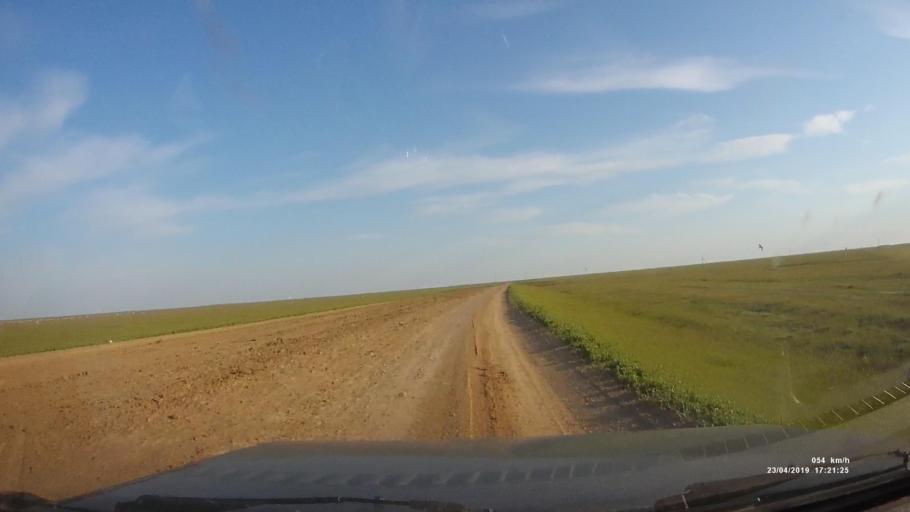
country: RU
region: Kalmykiya
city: Priyutnoye
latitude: 46.1763
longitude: 43.5053
